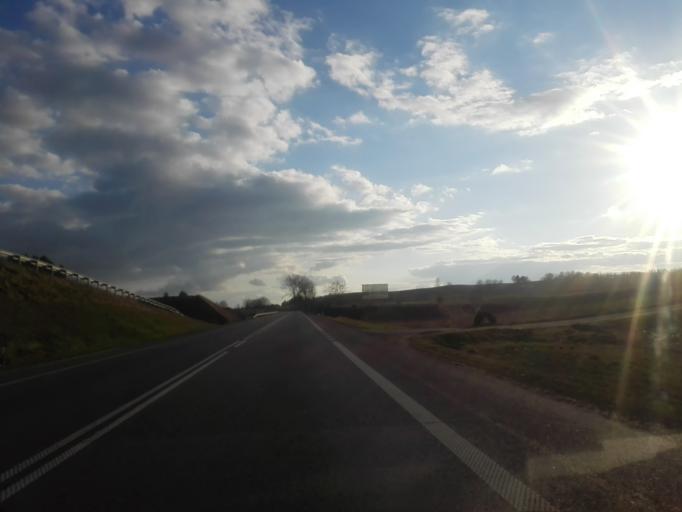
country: PL
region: Podlasie
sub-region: Suwalki
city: Suwalki
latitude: 54.1676
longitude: 22.9881
